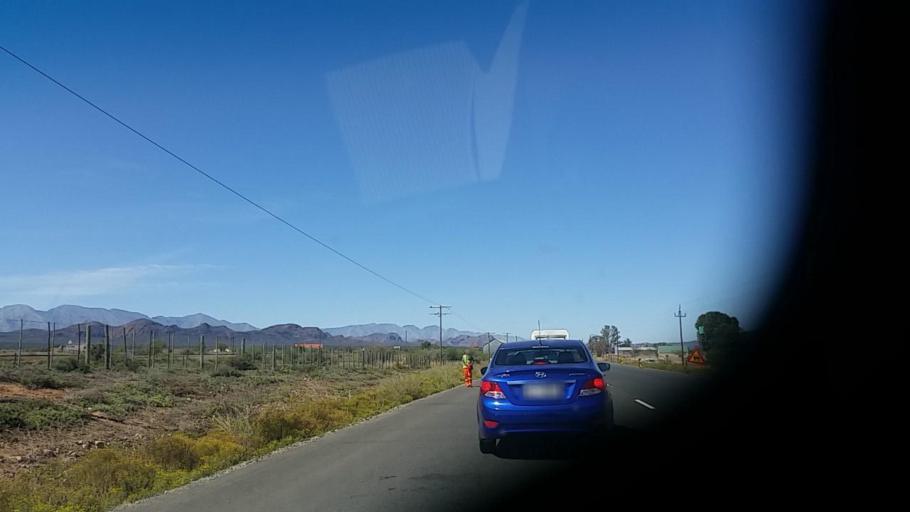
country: ZA
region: Western Cape
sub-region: Eden District Municipality
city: Oudtshoorn
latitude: -33.5819
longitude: 22.3089
